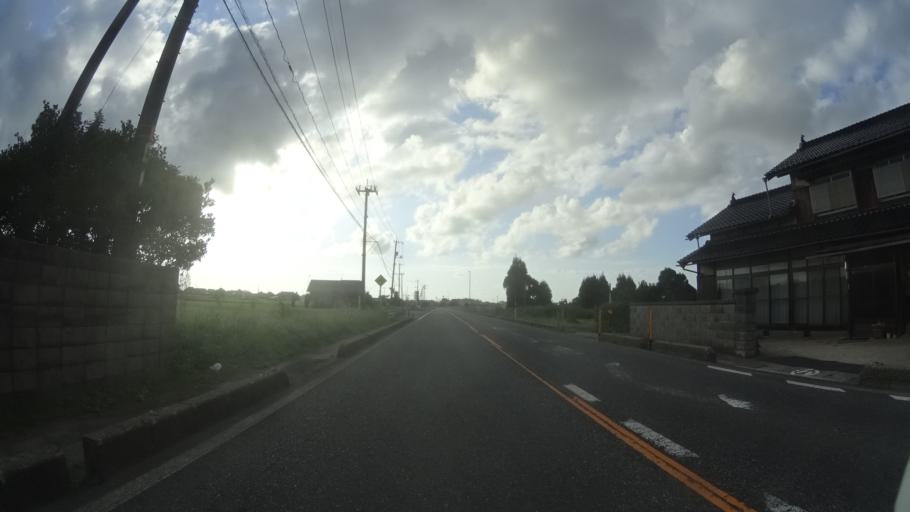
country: JP
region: Tottori
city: Kurayoshi
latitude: 35.5224
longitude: 133.5965
